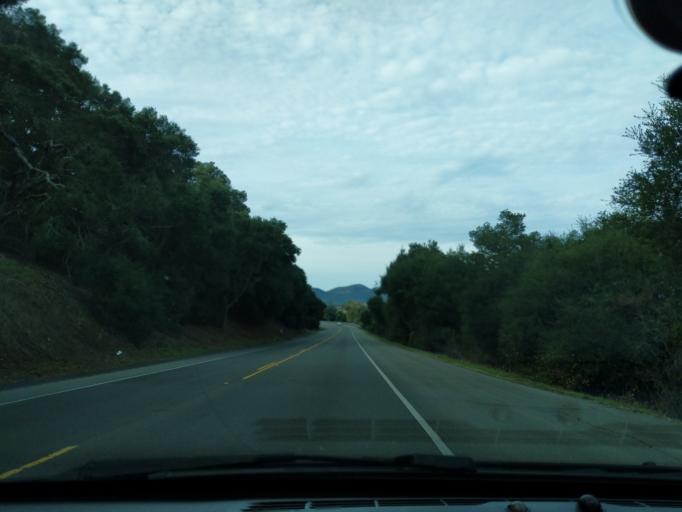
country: US
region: California
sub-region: Santa Barbara County
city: Solvang
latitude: 34.6041
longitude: -120.1184
